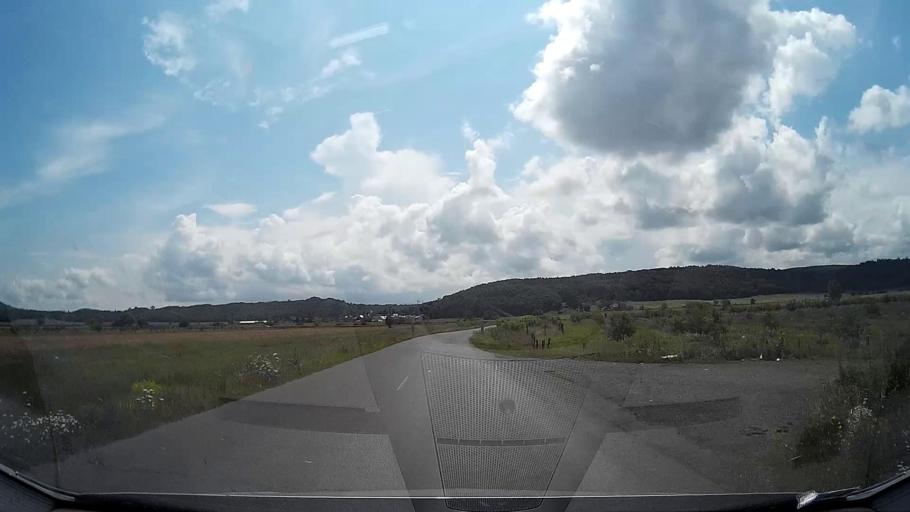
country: SK
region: Banskobystricky
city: Fil'akovo
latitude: 48.2954
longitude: 19.7907
